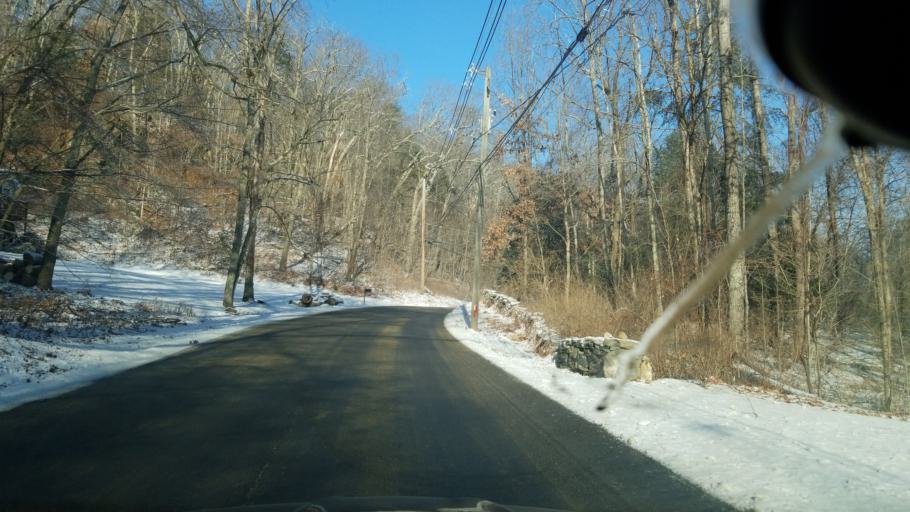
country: US
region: Connecticut
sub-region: Windham County
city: East Brooklyn
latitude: 41.8367
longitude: -71.9358
